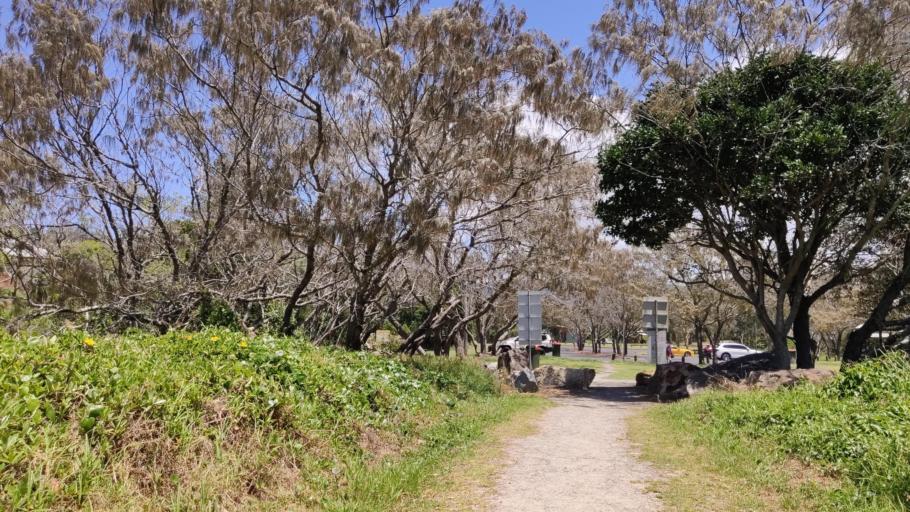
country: AU
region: New South Wales
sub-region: Port Macquarie-Hastings
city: North Haven
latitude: -31.6390
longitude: 152.8361
